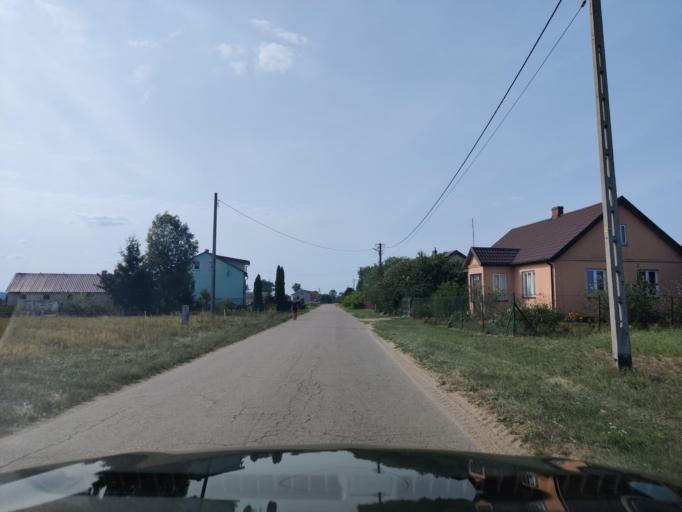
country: PL
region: Masovian Voivodeship
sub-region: Powiat pultuski
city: Obryte
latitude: 52.7630
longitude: 21.2947
